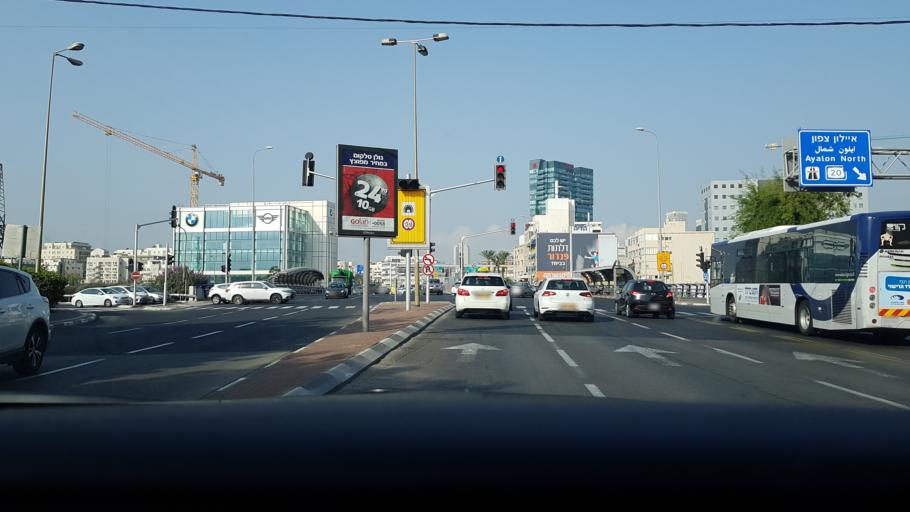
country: IL
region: Tel Aviv
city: Tel Aviv
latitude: 32.0593
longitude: 34.7875
